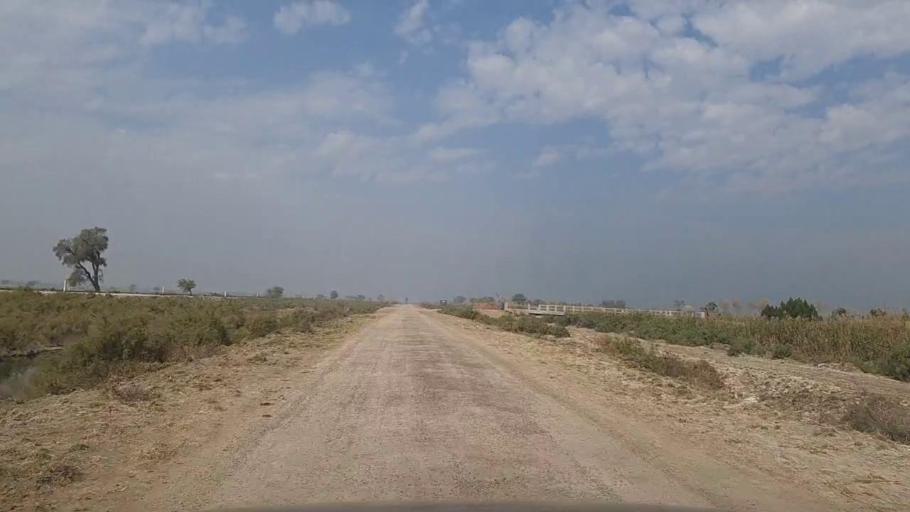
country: PK
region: Sindh
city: Daur
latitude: 26.3904
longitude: 68.3504
